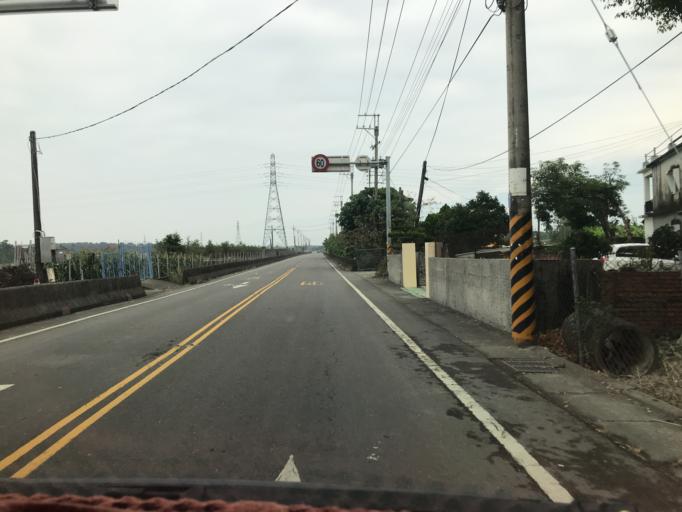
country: TW
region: Taiwan
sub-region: Pingtung
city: Pingtung
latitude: 22.5354
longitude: 120.5583
